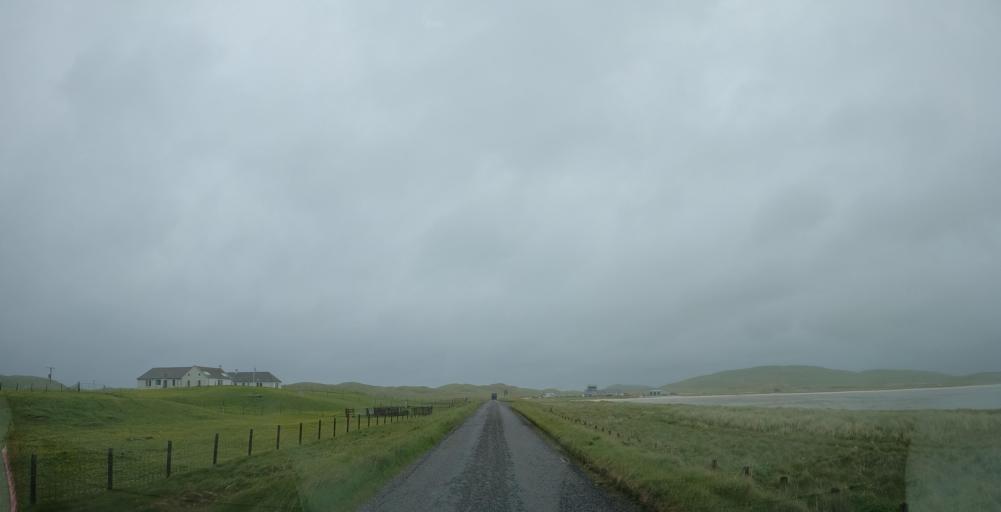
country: GB
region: Scotland
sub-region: Eilean Siar
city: Barra
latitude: 57.0221
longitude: -7.4489
